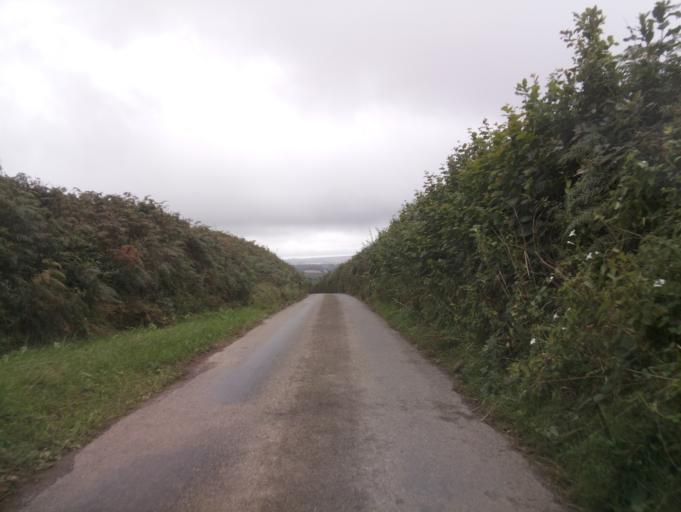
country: GB
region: England
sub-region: Devon
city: Kingsbridge
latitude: 50.2995
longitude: -3.7170
